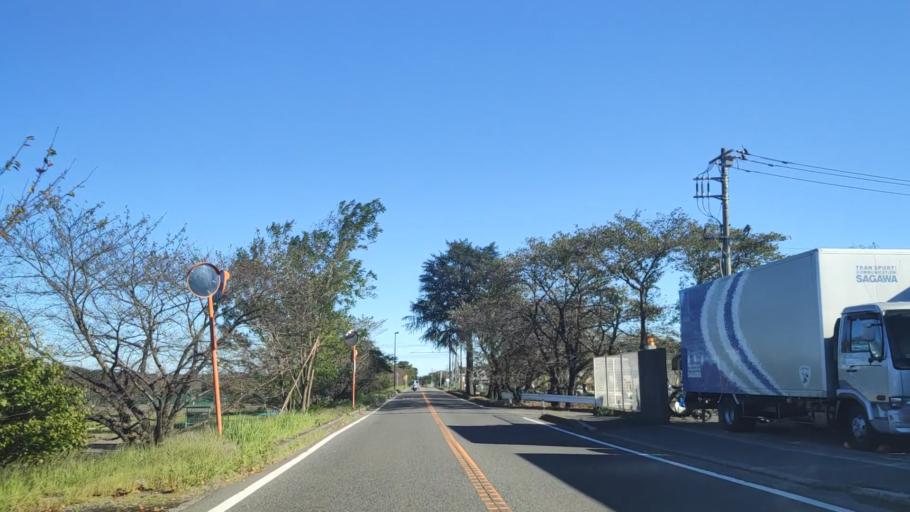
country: JP
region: Kanagawa
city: Zama
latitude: 35.5378
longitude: 139.3323
